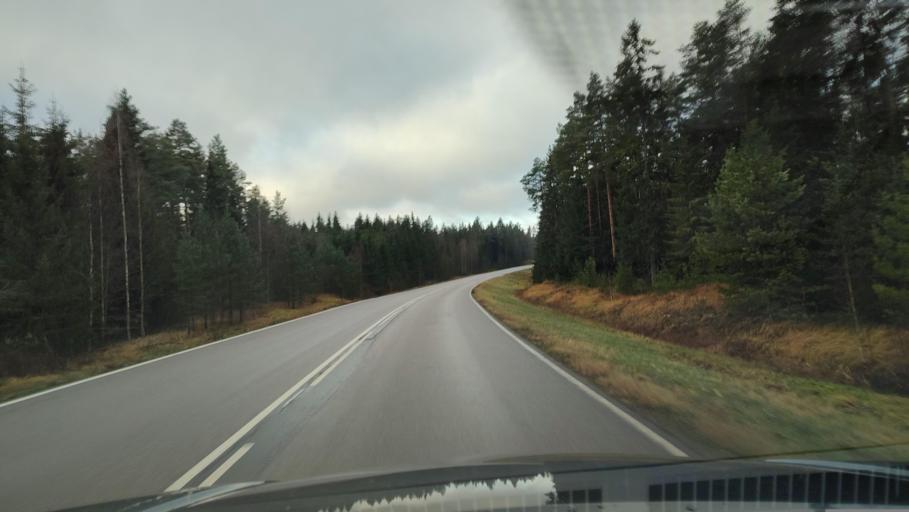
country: FI
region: Ostrobothnia
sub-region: Sydosterbotten
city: Kristinestad
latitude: 62.3049
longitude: 21.4398
